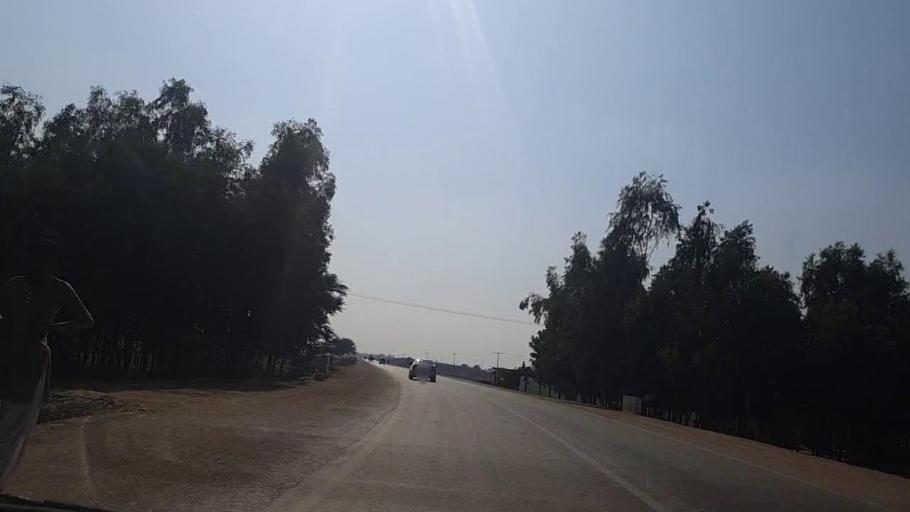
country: PK
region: Sindh
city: Hala
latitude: 25.9867
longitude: 68.3853
